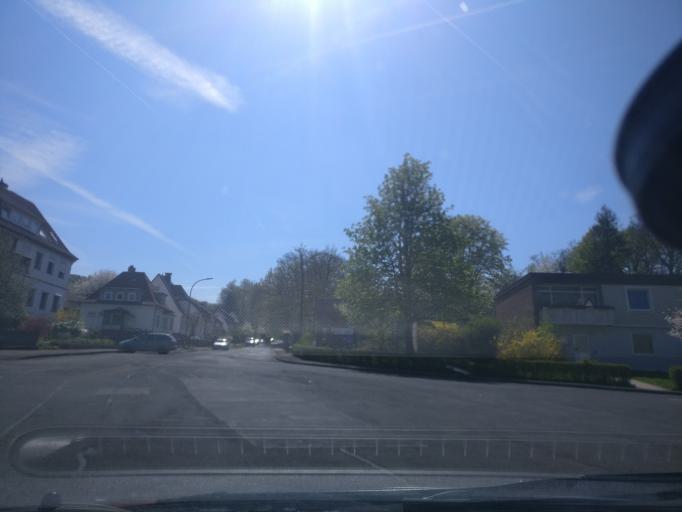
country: DE
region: Lower Saxony
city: Hannoversch Munden
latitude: 51.3997
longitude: 9.6264
